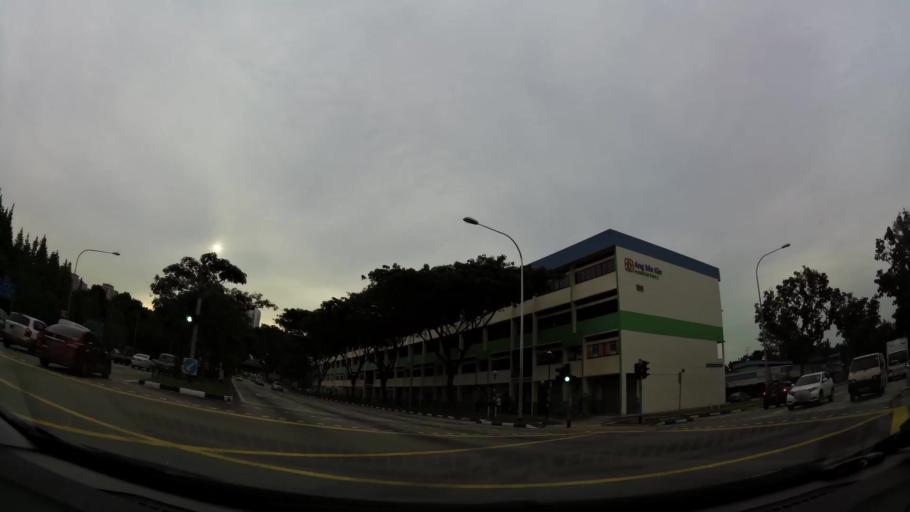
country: SG
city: Singapore
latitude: 1.3704
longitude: 103.8639
